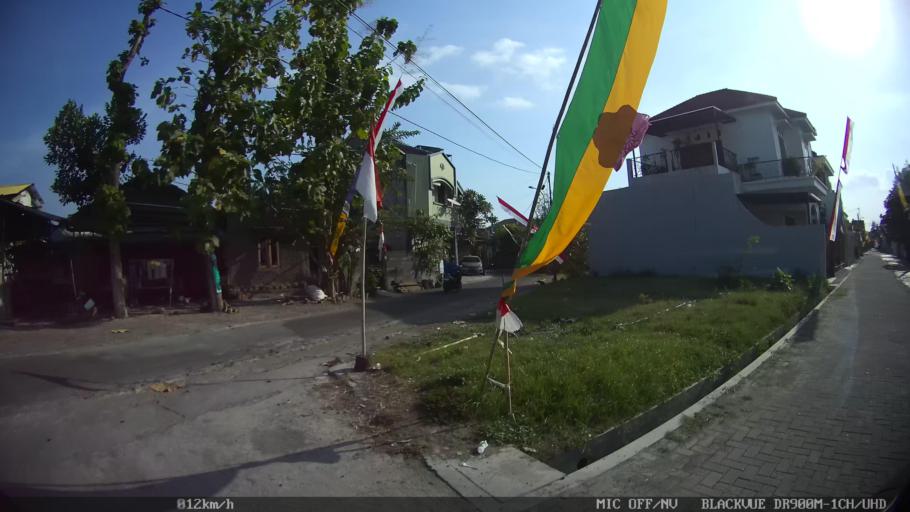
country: ID
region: Daerah Istimewa Yogyakarta
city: Yogyakarta
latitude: -7.8221
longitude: 110.3843
